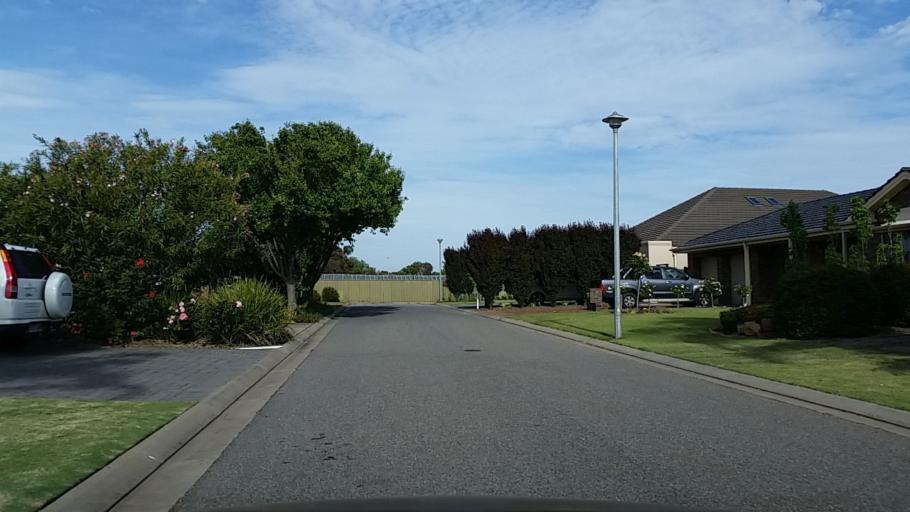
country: AU
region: South Australia
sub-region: Charles Sturt
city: Grange
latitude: -34.8968
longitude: 138.4996
